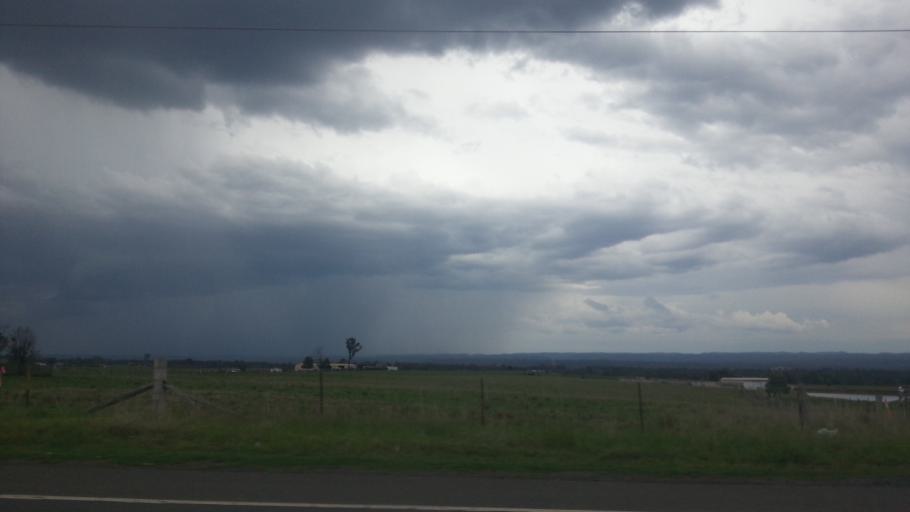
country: AU
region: New South Wales
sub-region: Liverpool
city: Luddenham
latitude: -33.8559
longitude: 150.6945
